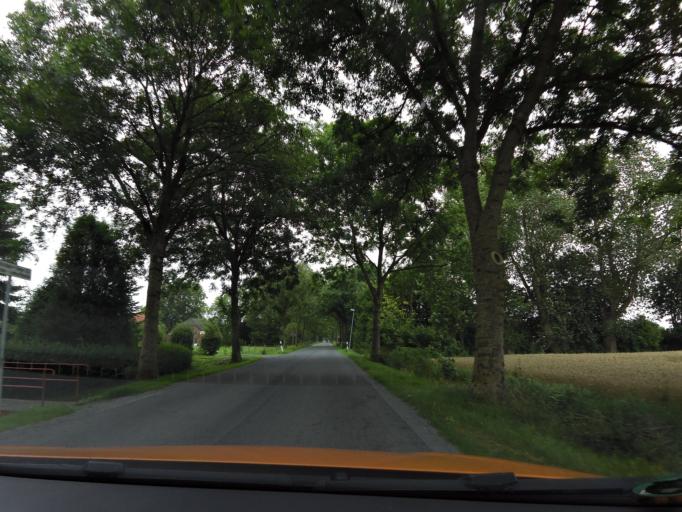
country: DE
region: Lower Saxony
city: Wirdum
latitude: 53.5040
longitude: 7.1647
